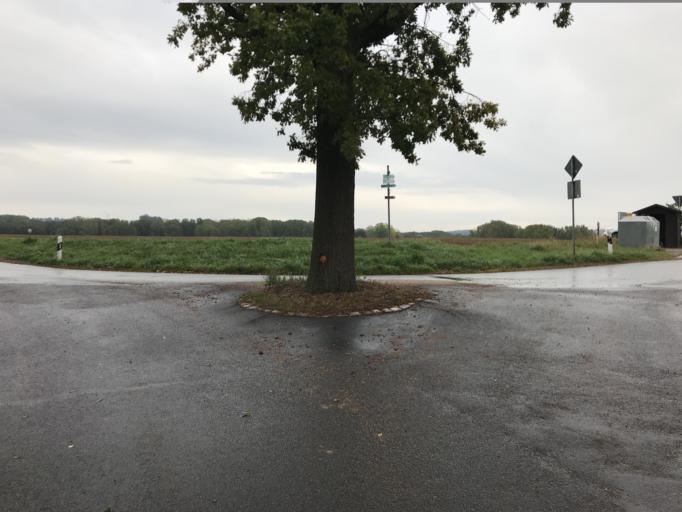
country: DE
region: Saxony
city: Seelitz
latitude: 51.0102
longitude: 12.8454
